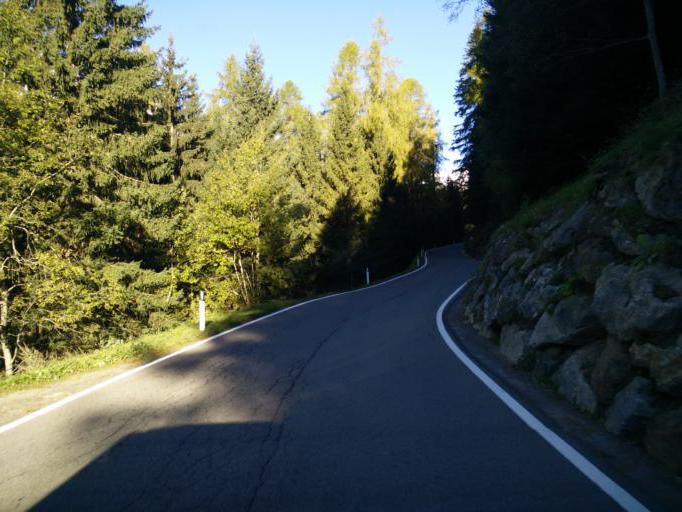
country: IT
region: Trentino-Alto Adige
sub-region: Bolzano
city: Moso in Passiria
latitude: 46.8533
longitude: 11.1620
